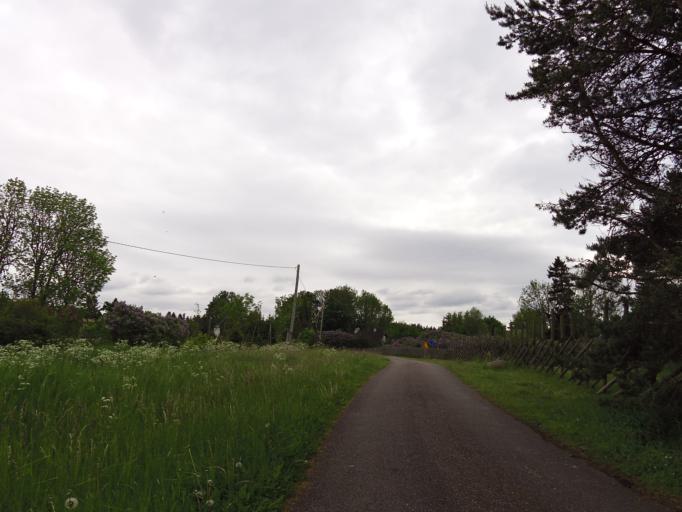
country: EE
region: Harju
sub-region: Paldiski linn
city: Paldiski
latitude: 59.2572
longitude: 23.7460
